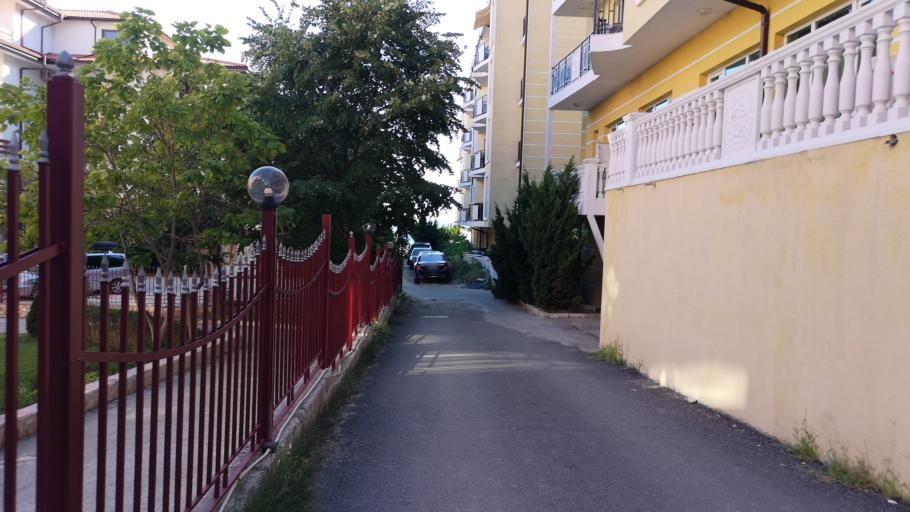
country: BG
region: Burgas
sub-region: Obshtina Nesebur
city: Sveti Vlas
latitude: 42.7034
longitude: 27.8069
